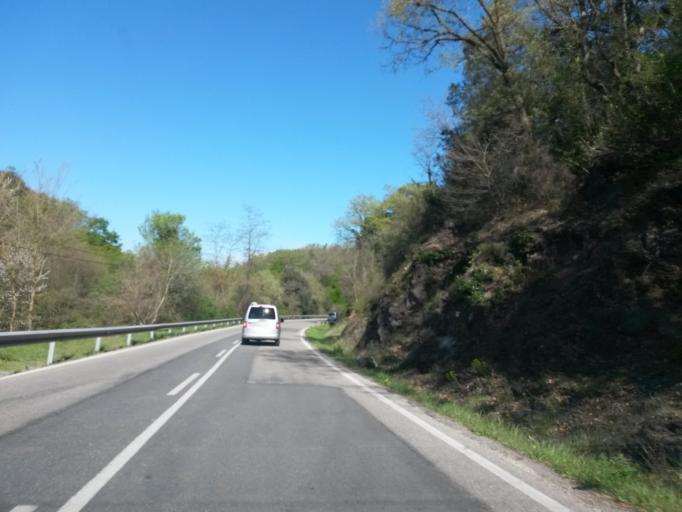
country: ES
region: Catalonia
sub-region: Provincia de Girona
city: Sant Cristofol de les Fonts
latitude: 42.1516
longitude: 2.5257
